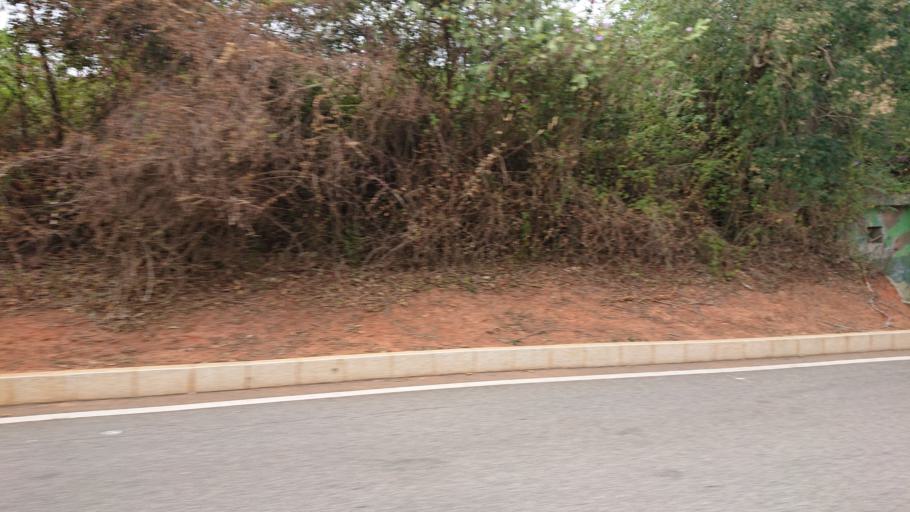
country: TW
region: Fukien
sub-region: Kinmen
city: Jincheng
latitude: 24.4385
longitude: 118.2494
